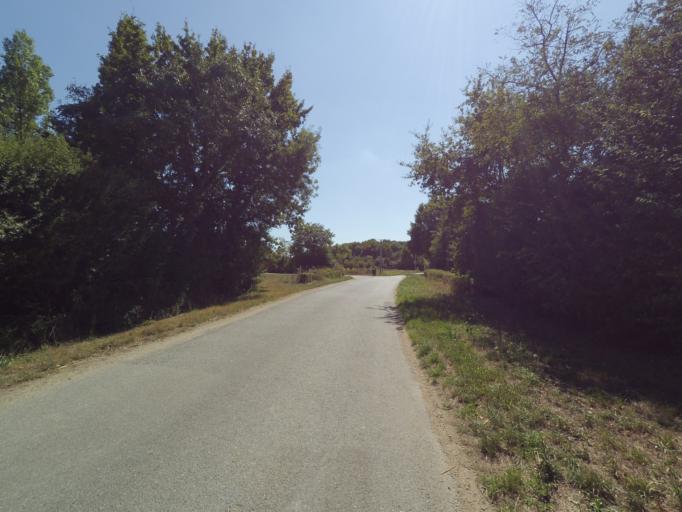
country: FR
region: Pays de la Loire
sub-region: Departement de la Loire-Atlantique
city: Vieillevigne
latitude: 46.9822
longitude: -1.4241
